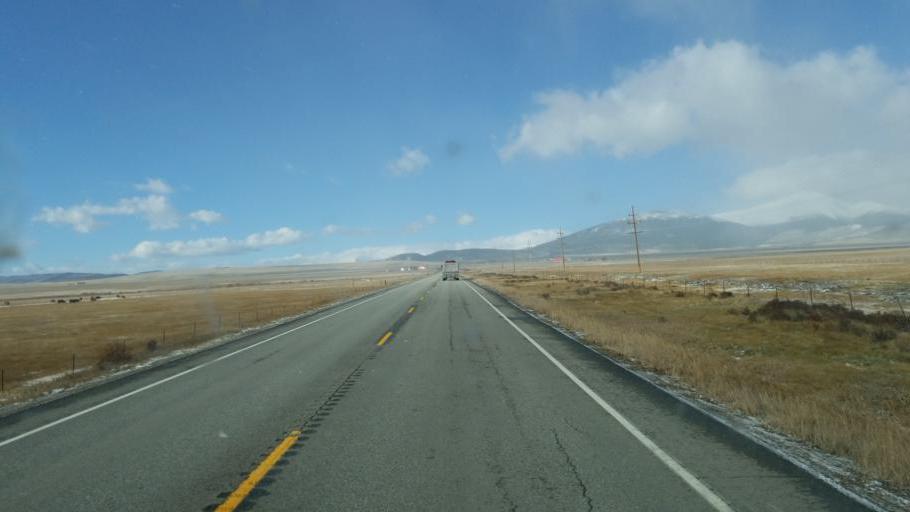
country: US
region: Colorado
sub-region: Park County
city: Fairplay
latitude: 39.3541
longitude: -105.8250
